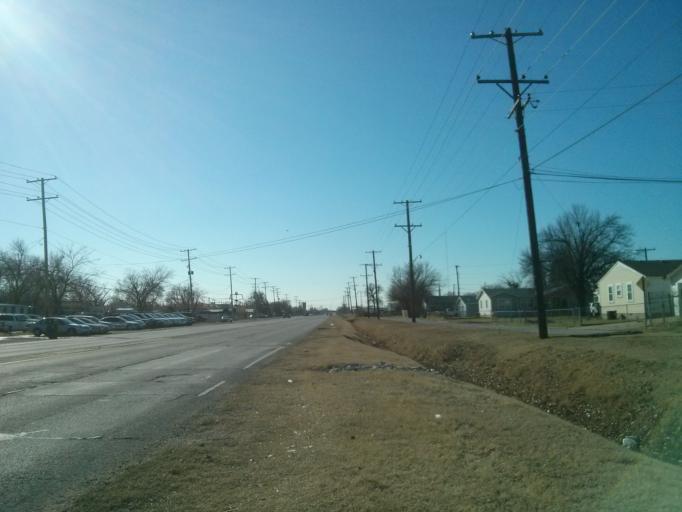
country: US
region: Oklahoma
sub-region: Tulsa County
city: Owasso
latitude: 36.1754
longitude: -95.8689
